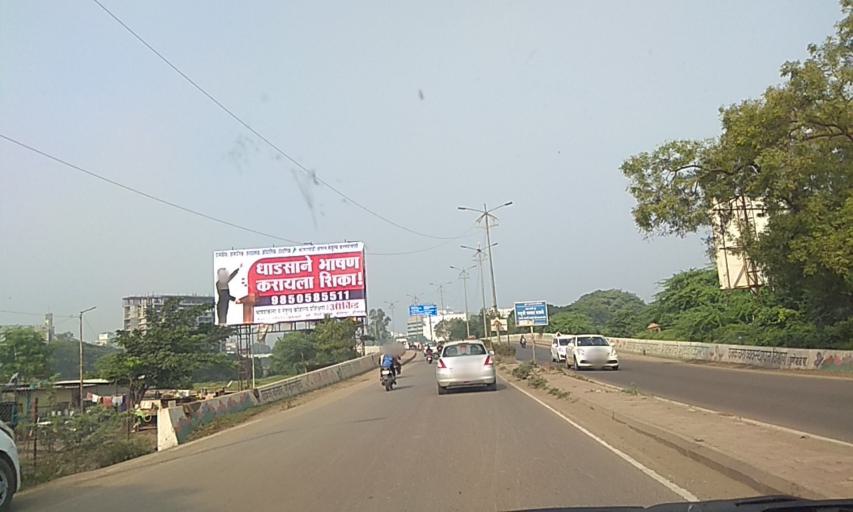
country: IN
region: Maharashtra
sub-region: Pune Division
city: Shivaji Nagar
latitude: 18.5328
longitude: 73.8587
